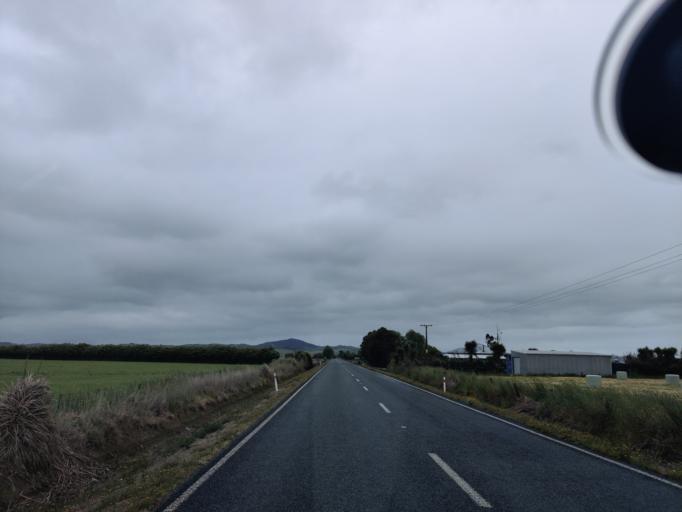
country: NZ
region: Northland
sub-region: Kaipara District
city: Dargaville
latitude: -36.1231
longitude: 174.0511
